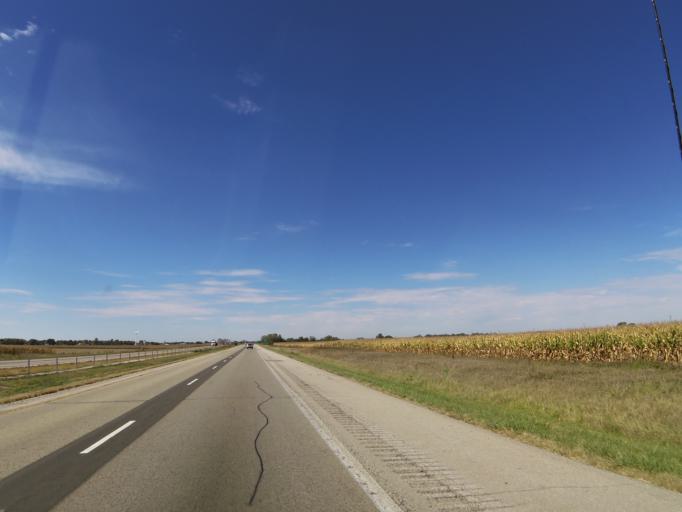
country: US
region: Illinois
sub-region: Champaign County
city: Homer
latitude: 40.1203
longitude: -87.9408
